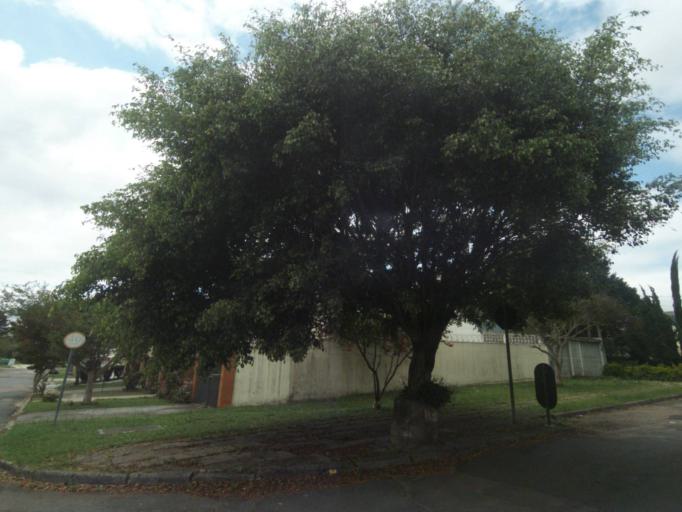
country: BR
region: Parana
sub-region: Pinhais
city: Pinhais
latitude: -25.4054
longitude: -49.2228
